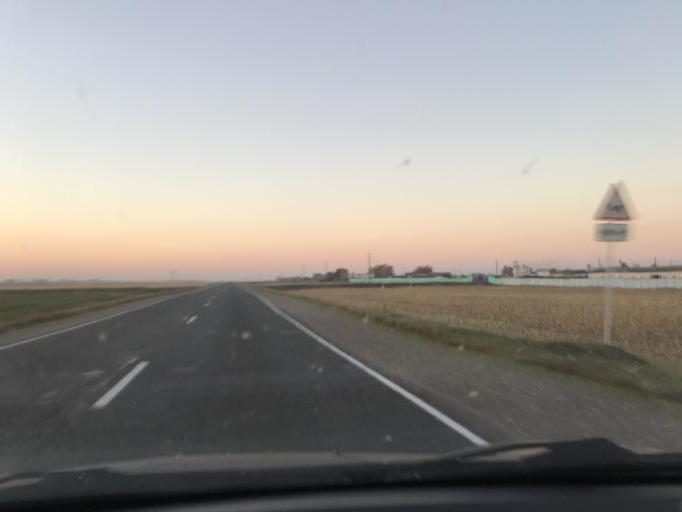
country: BY
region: Gomel
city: Horad Rechytsa
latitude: 52.2477
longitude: 30.4973
